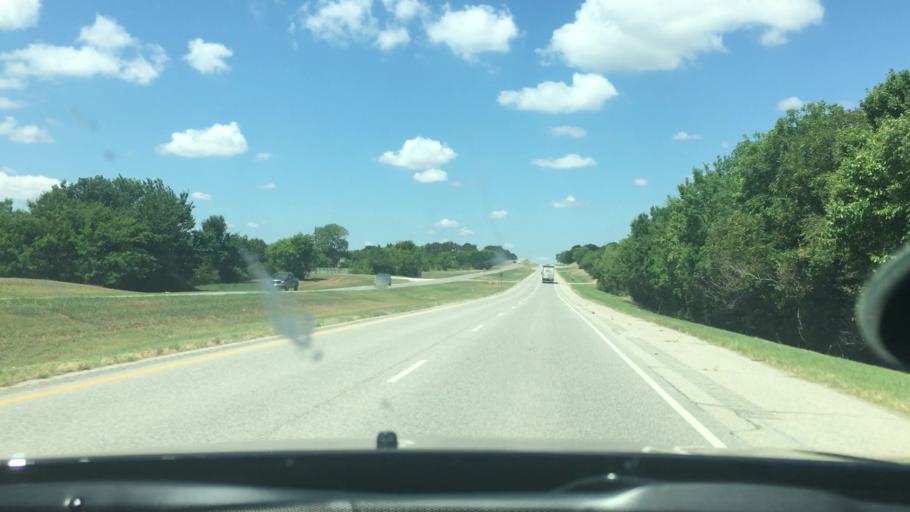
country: US
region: Oklahoma
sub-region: Carter County
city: Wilson
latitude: 34.1730
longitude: -97.3978
